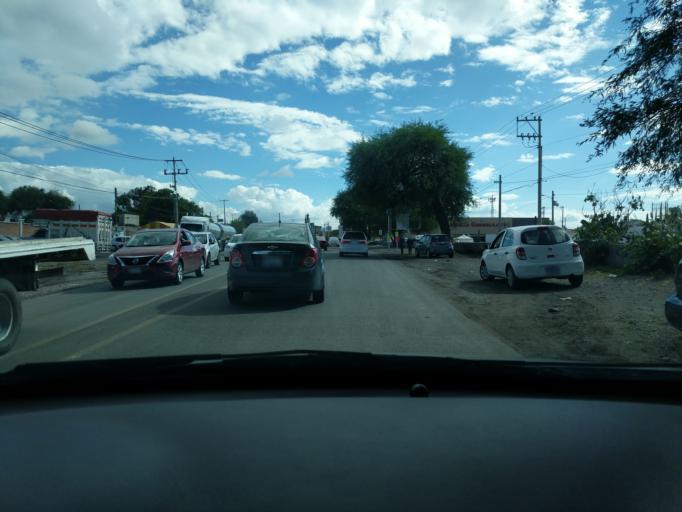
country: MX
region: Queretaro
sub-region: El Marques
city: General Lazaro Cardenas (El Colorado)
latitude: 20.5814
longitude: -100.2535
